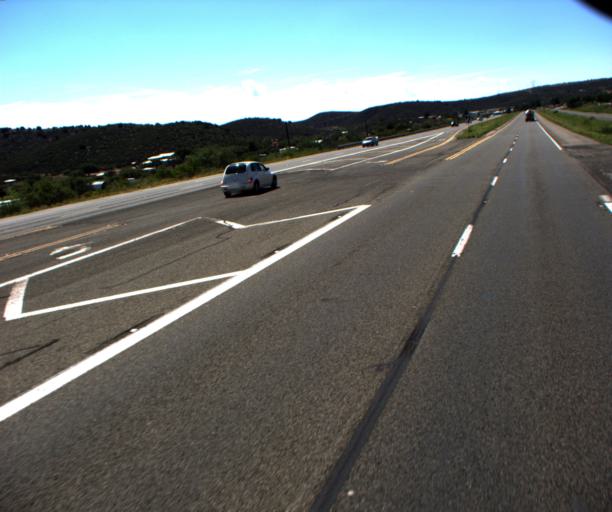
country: US
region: Arizona
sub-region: Yavapai County
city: Mayer
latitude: 34.3941
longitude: -112.2228
